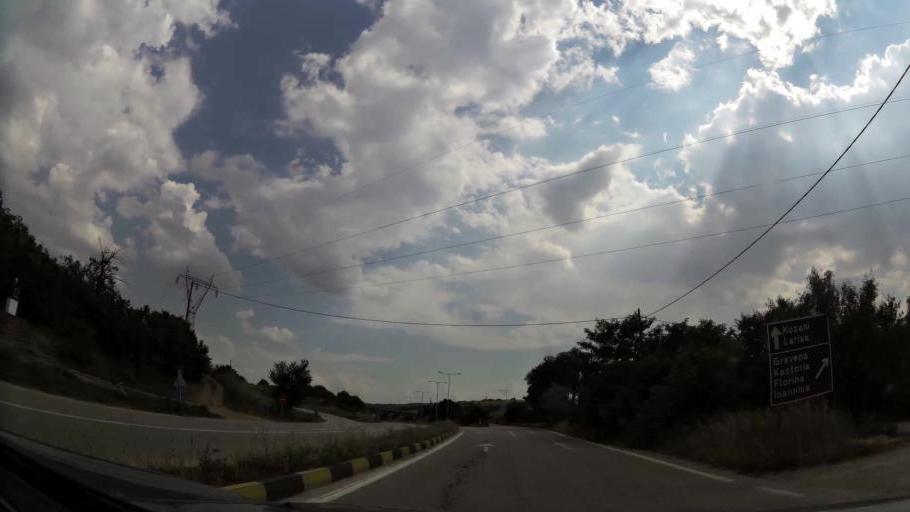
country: GR
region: West Macedonia
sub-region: Nomos Kozanis
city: Koila
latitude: 40.3444
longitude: 21.8253
